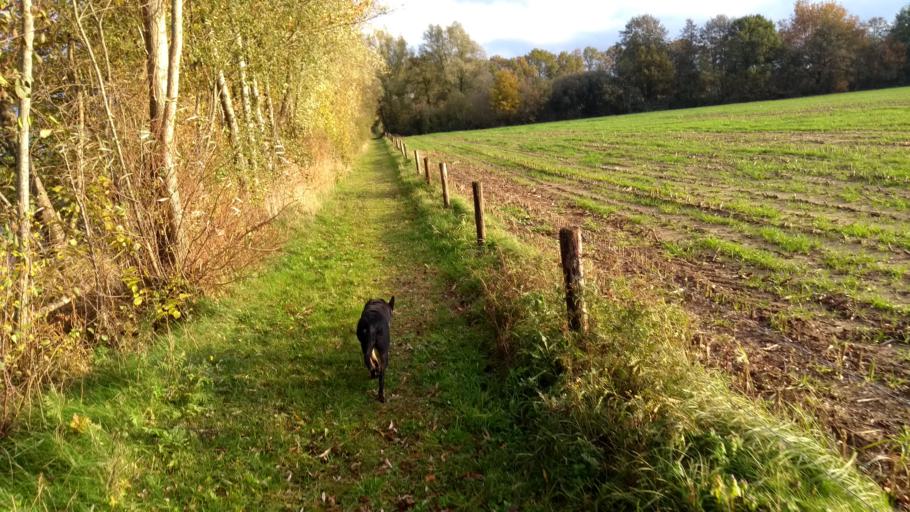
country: NL
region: Overijssel
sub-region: Gemeente Borne
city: Borne
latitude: 52.3420
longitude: 6.7186
